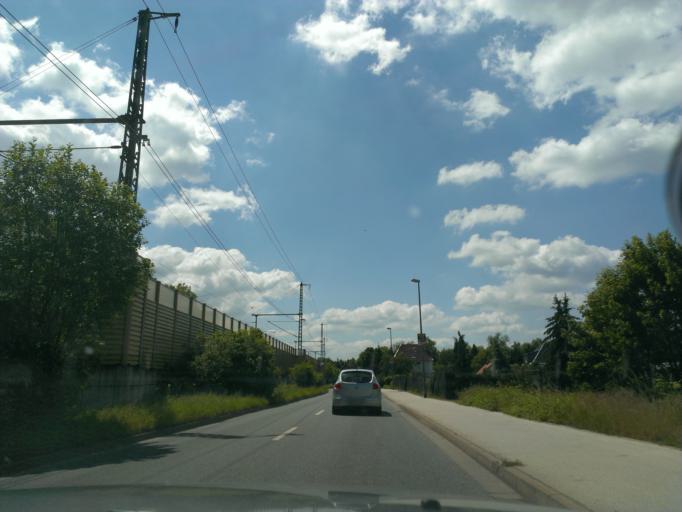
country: DE
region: Thuringia
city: Erfurt
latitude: 50.9585
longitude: 11.0079
